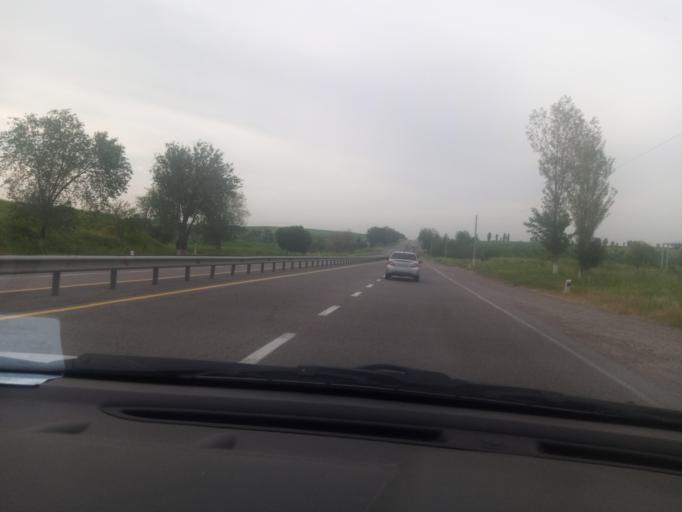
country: UZ
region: Toshkent
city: Tuytepa
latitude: 41.0604
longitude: 69.4840
